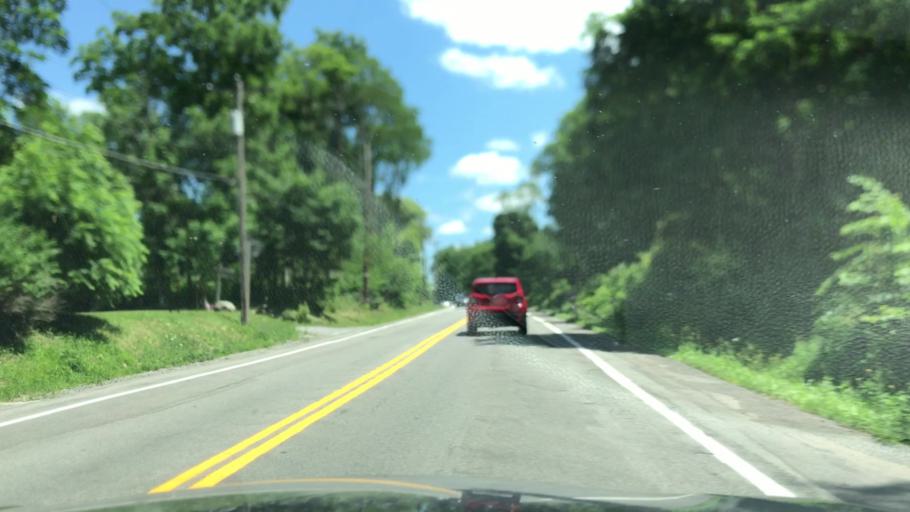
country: US
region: New York
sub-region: Erie County
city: East Aurora
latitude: 42.7674
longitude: -78.5864
